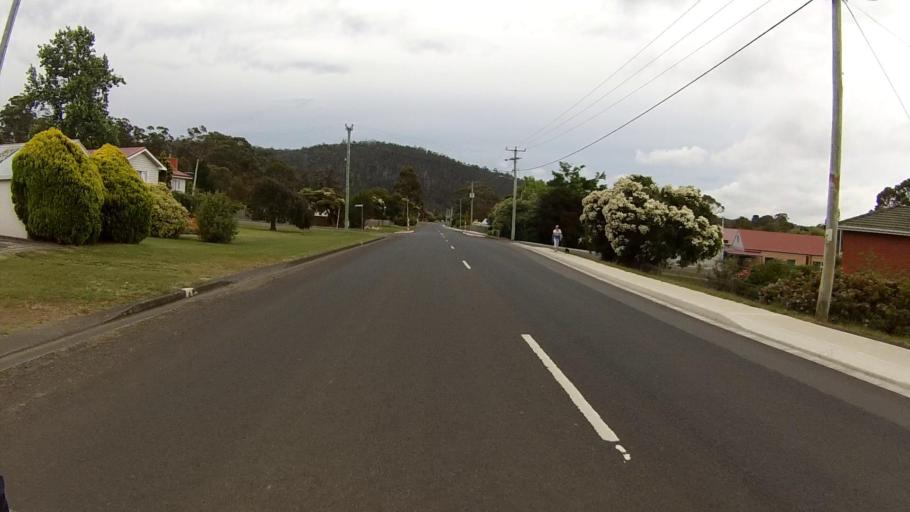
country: AU
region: Tasmania
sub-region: Sorell
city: Sorell
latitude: -42.5638
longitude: 147.8730
